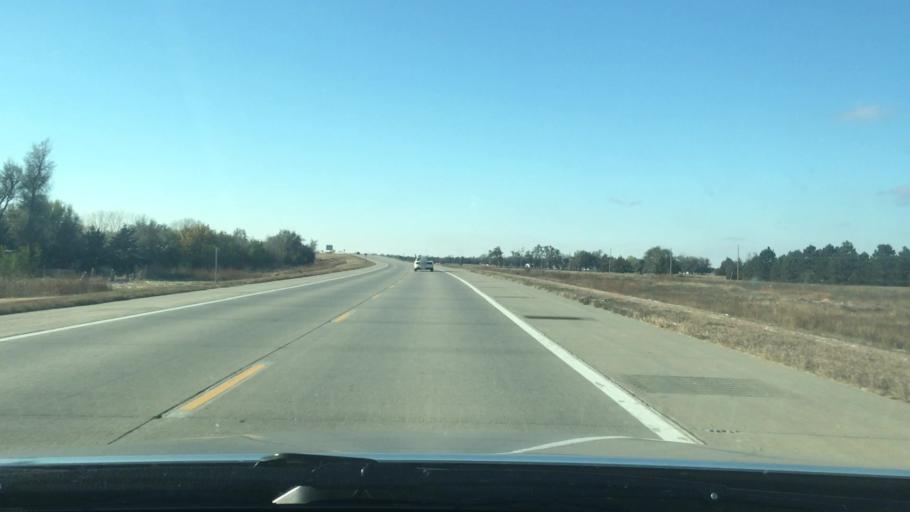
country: US
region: Kansas
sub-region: Reno County
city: Hutchinson
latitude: 38.0989
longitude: -98.0080
